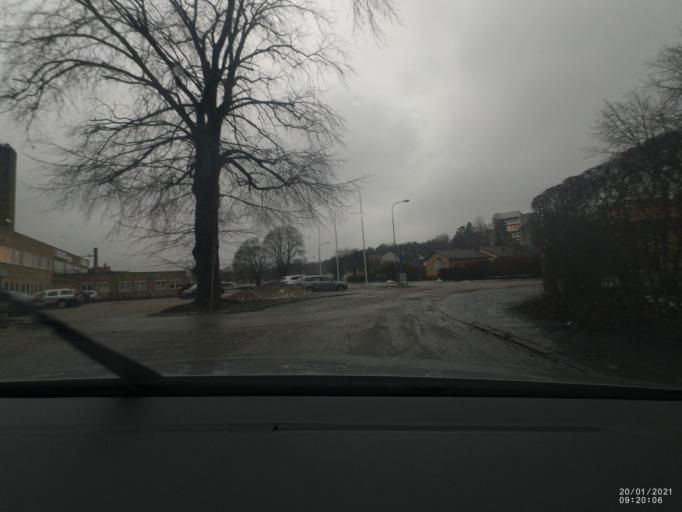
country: SE
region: Soedermanland
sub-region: Nykopings Kommun
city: Nykoping
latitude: 58.7573
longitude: 16.9945
